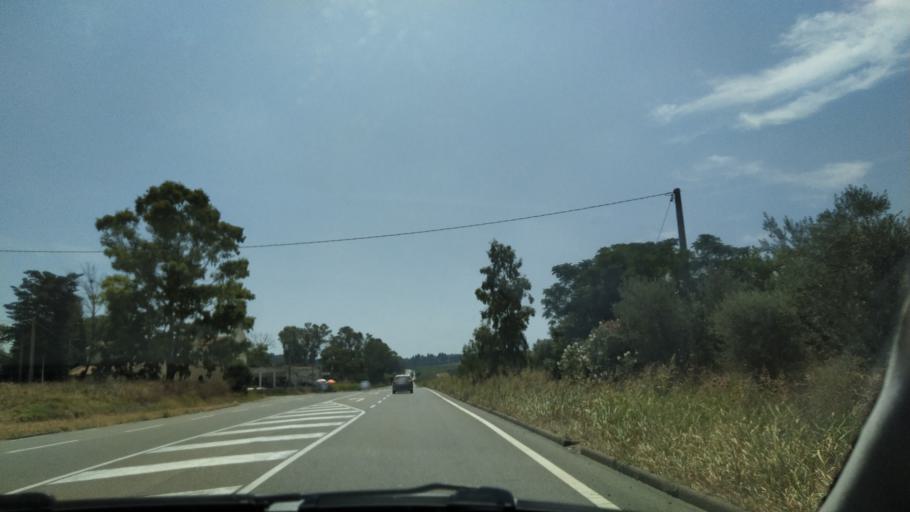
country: IT
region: Basilicate
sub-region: Provincia di Matera
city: Bernalda
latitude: 40.4447
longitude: 16.7796
